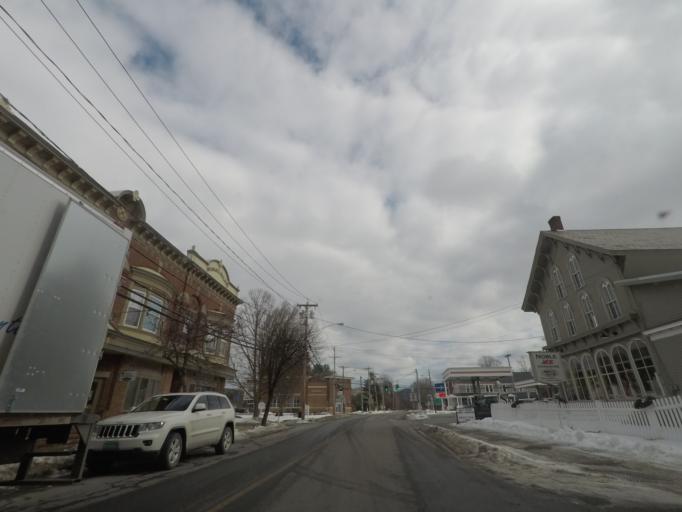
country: US
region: New York
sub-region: Washington County
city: Cambridge
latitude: 43.0278
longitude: -73.3772
